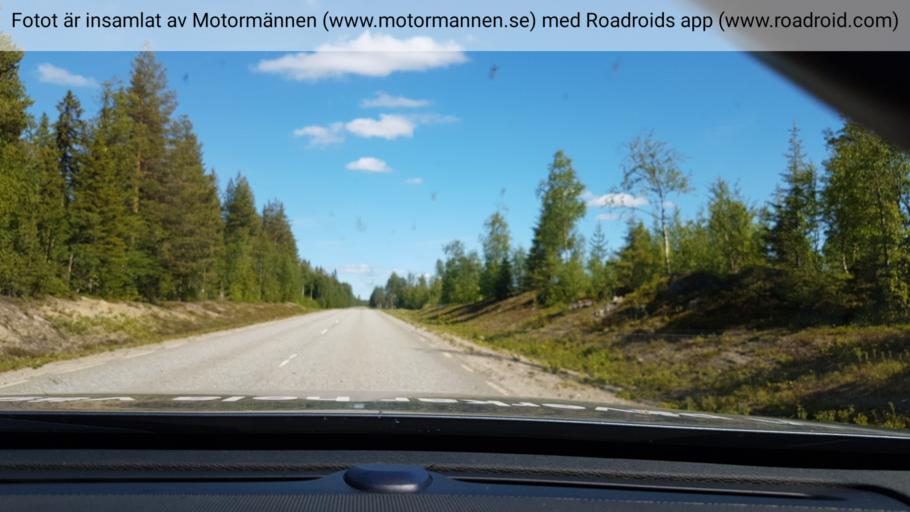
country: SE
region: Vaesterbotten
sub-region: Lycksele Kommun
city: Soderfors
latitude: 64.6335
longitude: 17.9542
